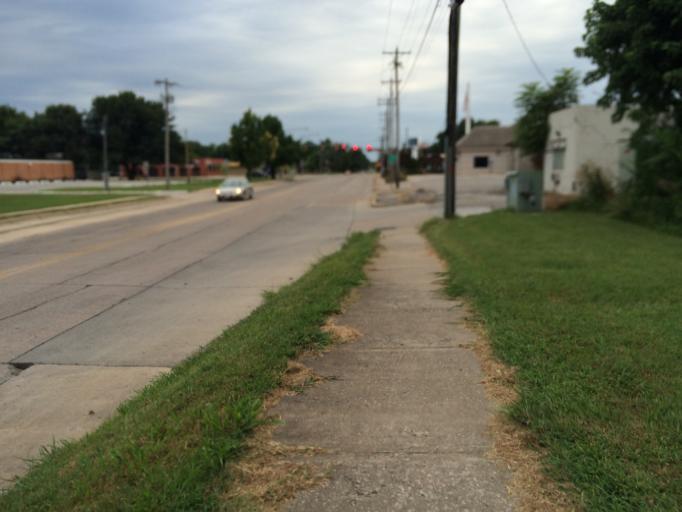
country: US
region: Oklahoma
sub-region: Cleveland County
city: Norman
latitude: 35.2197
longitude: -97.4591
